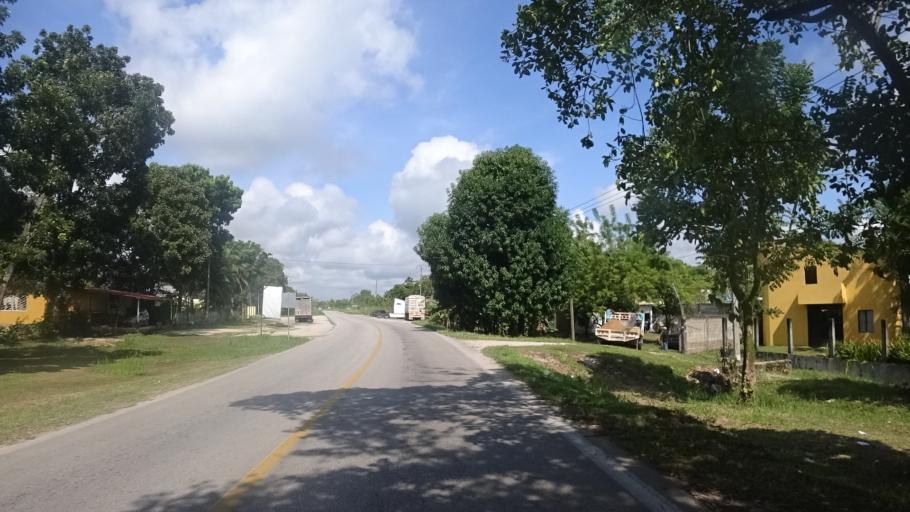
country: MX
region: Chiapas
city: Palenque
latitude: 17.5519
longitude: -91.9868
